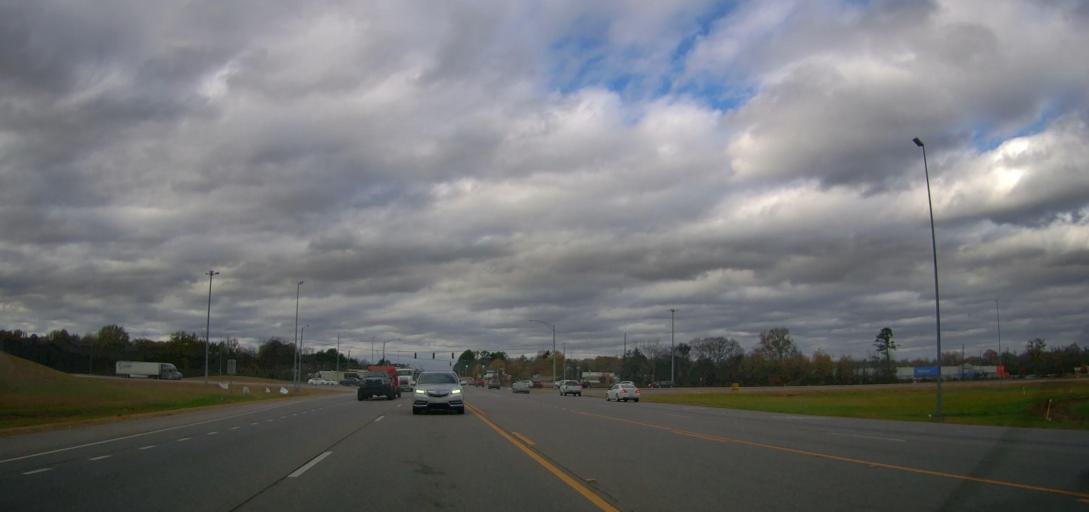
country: US
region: Alabama
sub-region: Lawrence County
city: Moulton
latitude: 34.4913
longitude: -87.2783
